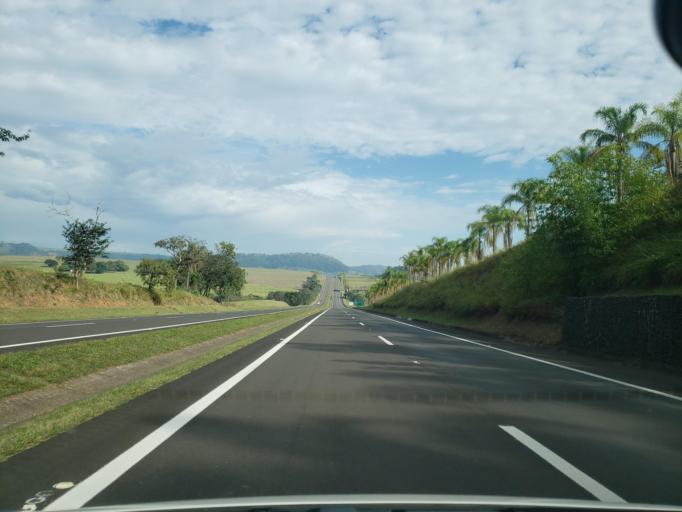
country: BR
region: Sao Paulo
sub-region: Dois Corregos
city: Dois Corregos
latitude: -22.2445
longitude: -48.3078
